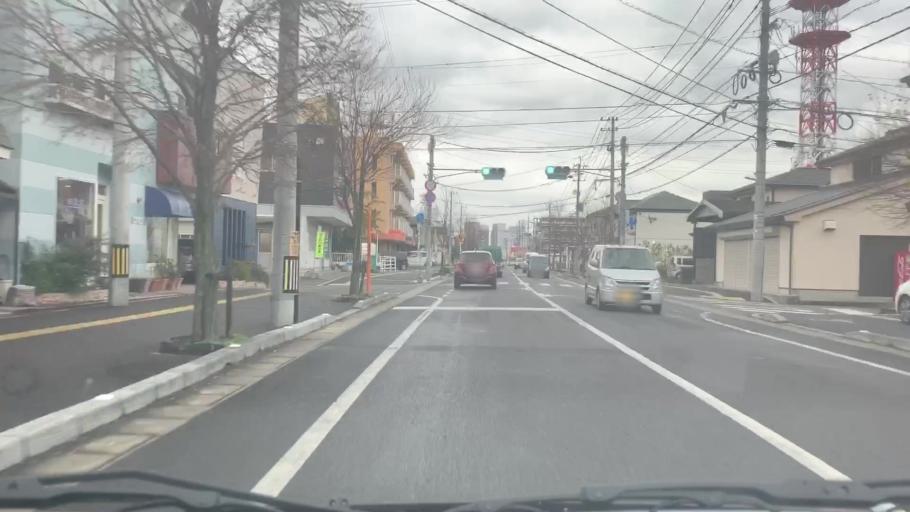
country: JP
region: Saga Prefecture
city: Saga-shi
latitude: 33.2637
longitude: 130.2887
